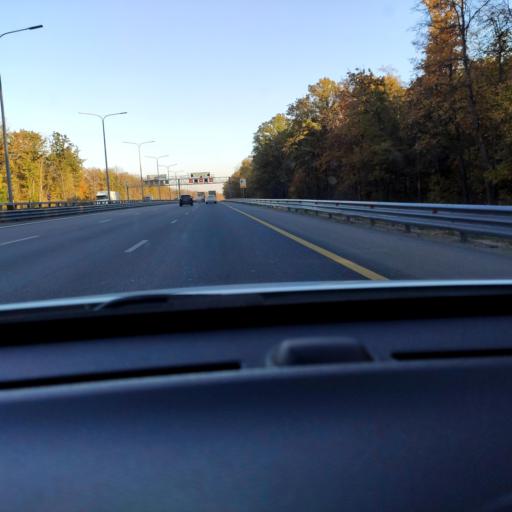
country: RU
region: Voronezj
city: Podgornoye
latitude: 51.8348
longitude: 39.2307
